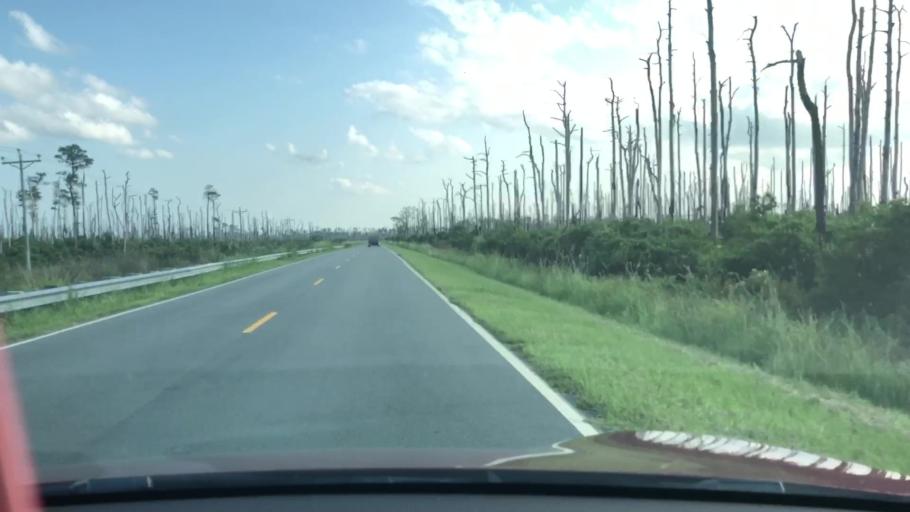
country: US
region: North Carolina
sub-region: Dare County
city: Wanchese
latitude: 35.6373
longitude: -75.7791
